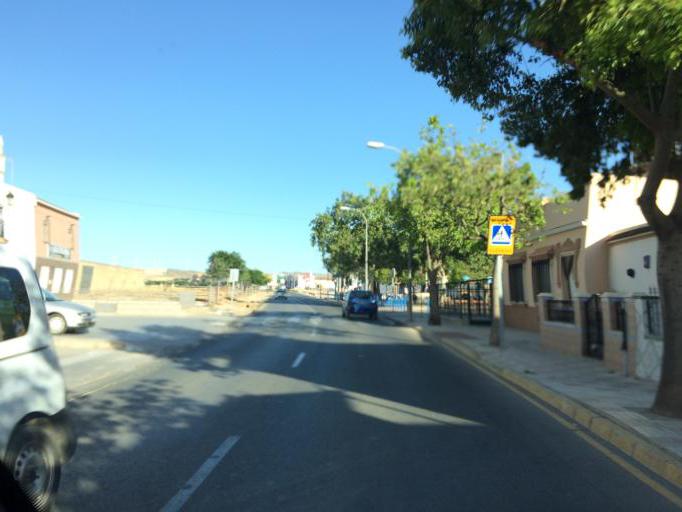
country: ES
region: Andalusia
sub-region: Provincia de Malaga
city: Campillos
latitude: 37.0484
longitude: -4.8674
